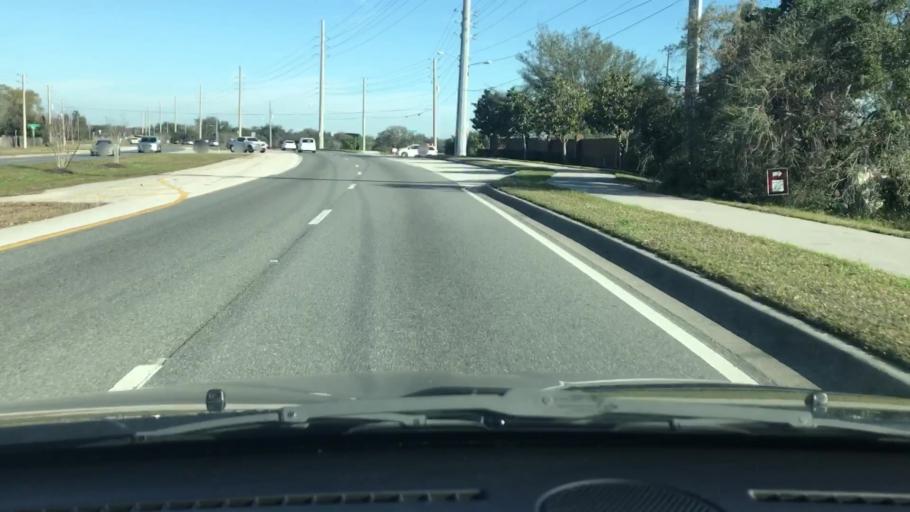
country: US
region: Florida
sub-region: Osceola County
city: Campbell
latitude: 28.2343
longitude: -81.4338
